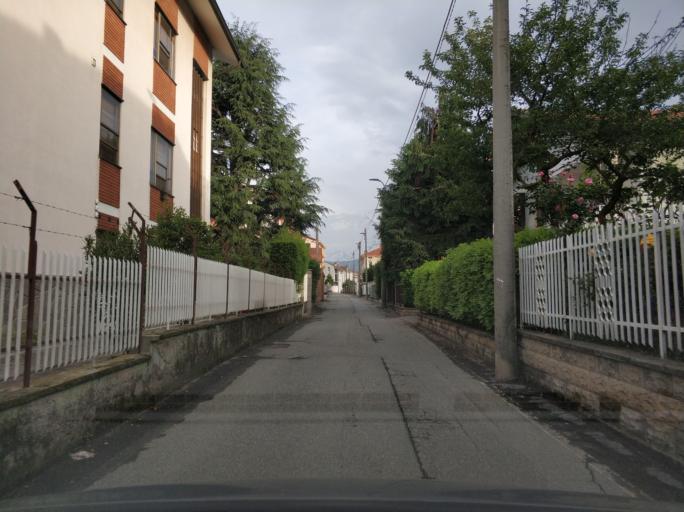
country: IT
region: Piedmont
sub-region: Provincia di Torino
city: San Carlo Canavese
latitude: 45.2380
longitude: 7.6067
